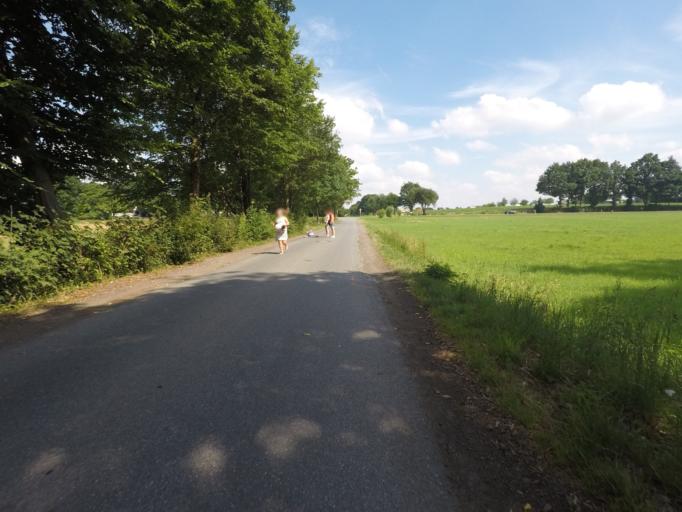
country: DE
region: North Rhine-Westphalia
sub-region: Regierungsbezirk Detmold
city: Hiddenhausen
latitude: 52.1513
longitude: 8.5949
